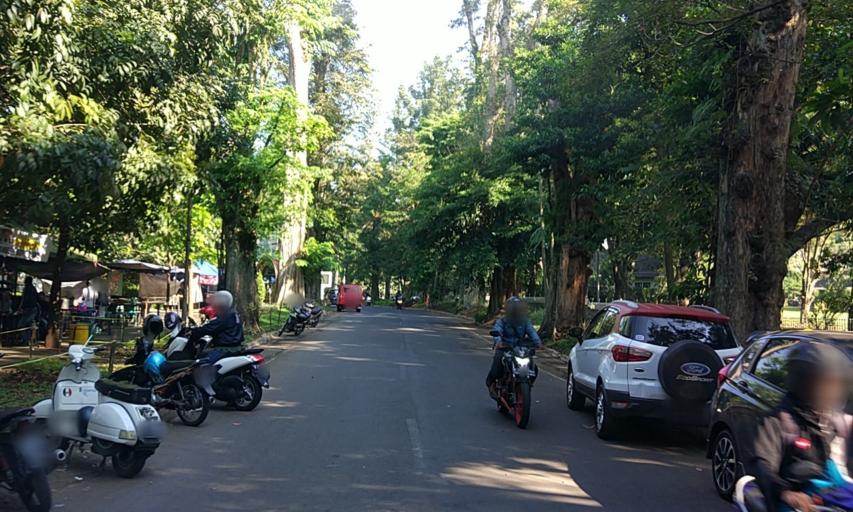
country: ID
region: West Java
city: Bandung
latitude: -6.8934
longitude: 107.6118
